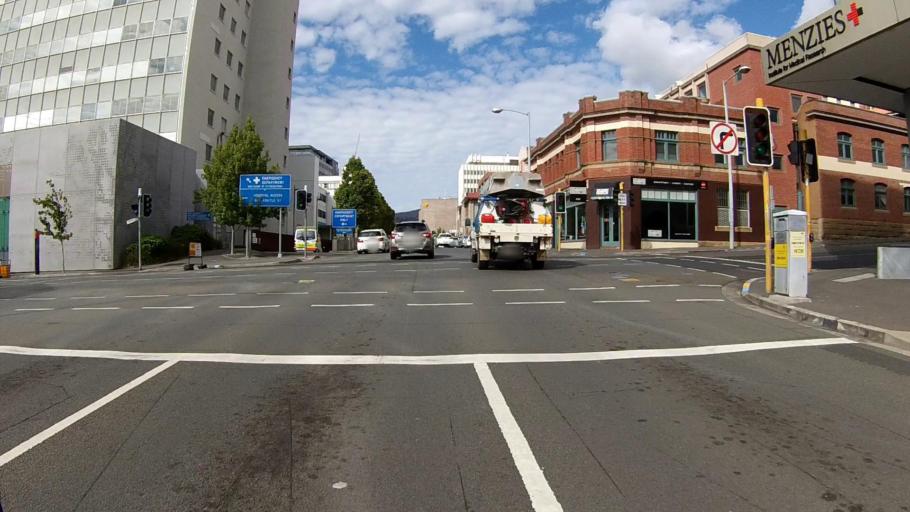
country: AU
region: Tasmania
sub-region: Hobart
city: Hobart
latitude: -42.8789
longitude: 147.3300
